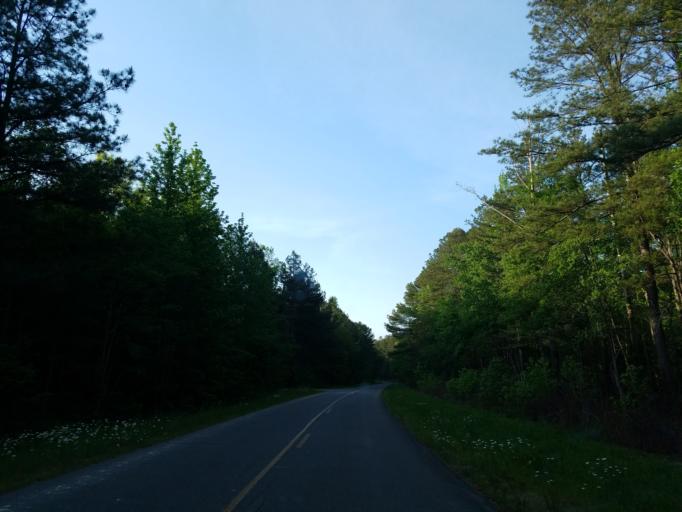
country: US
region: Georgia
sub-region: Gordon County
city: Calhoun
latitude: 34.6054
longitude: -85.0814
